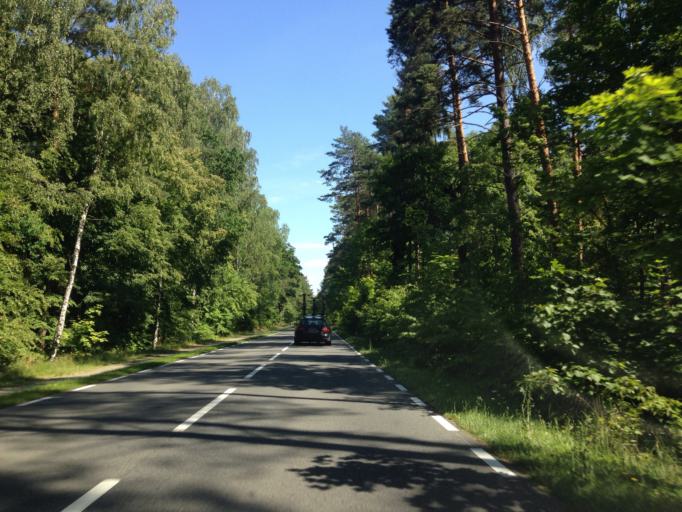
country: PL
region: Kujawsko-Pomorskie
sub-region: Powiat swiecki
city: Osie
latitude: 53.6078
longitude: 18.3116
